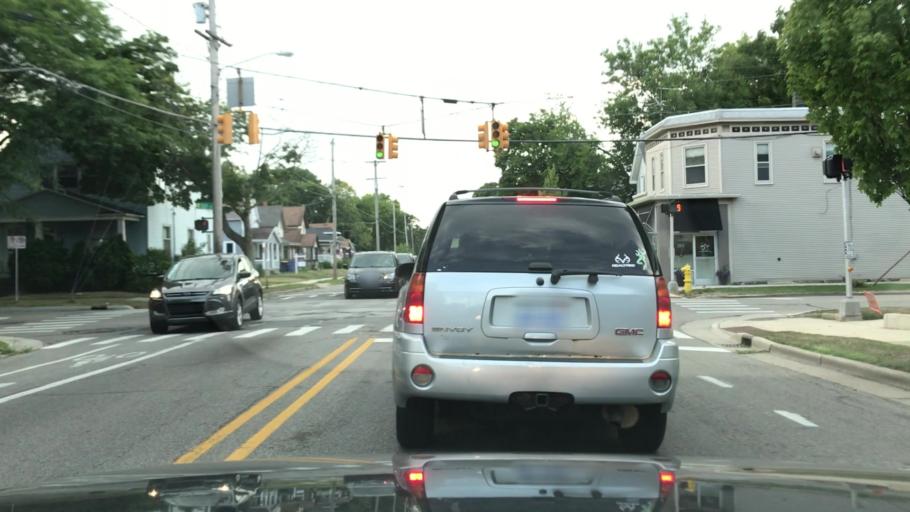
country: US
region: Michigan
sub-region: Kent County
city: Grand Rapids
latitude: 42.9955
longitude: -85.6643
